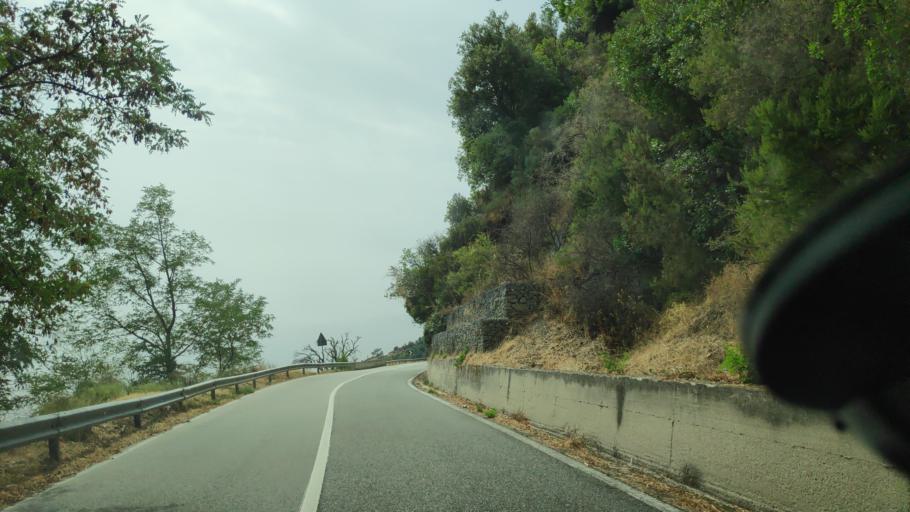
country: IT
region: Calabria
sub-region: Provincia di Catanzaro
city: San Sostene
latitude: 38.6411
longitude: 16.5122
